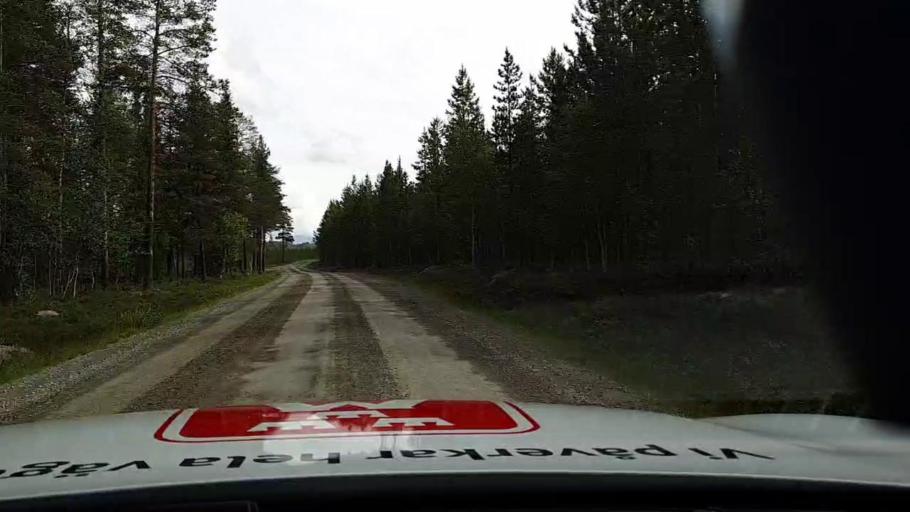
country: SE
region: Jaemtland
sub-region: Are Kommun
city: Jarpen
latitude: 62.4951
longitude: 13.5046
